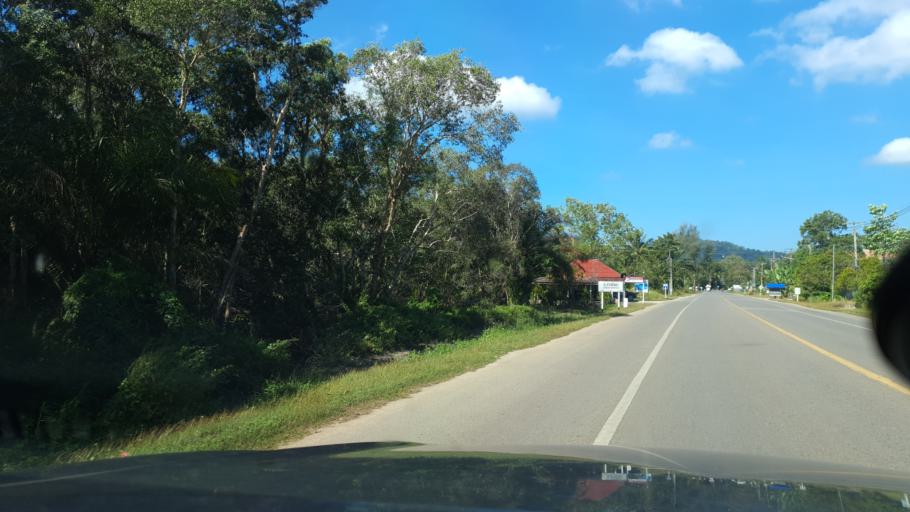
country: TH
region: Krabi
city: Krabi
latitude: 8.0268
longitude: 98.8751
